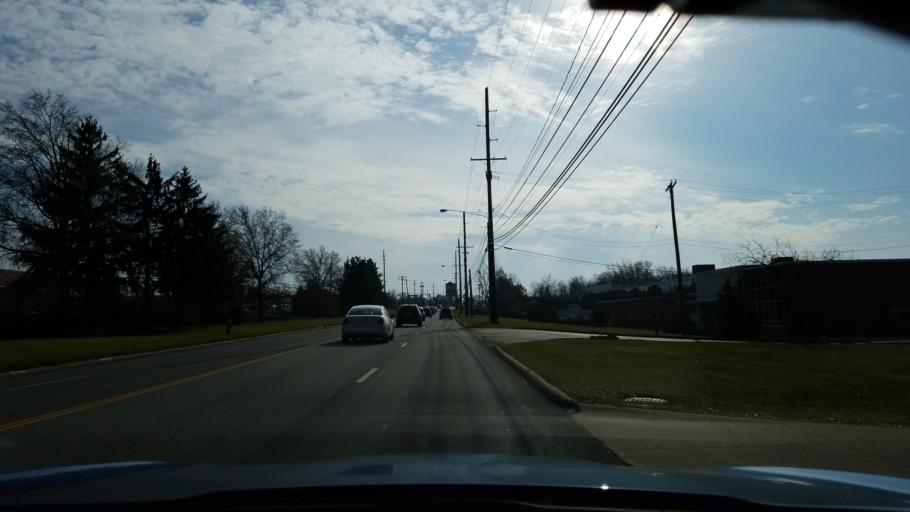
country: US
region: Ohio
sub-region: Summit County
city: Northfield
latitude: 41.3533
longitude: -81.5267
